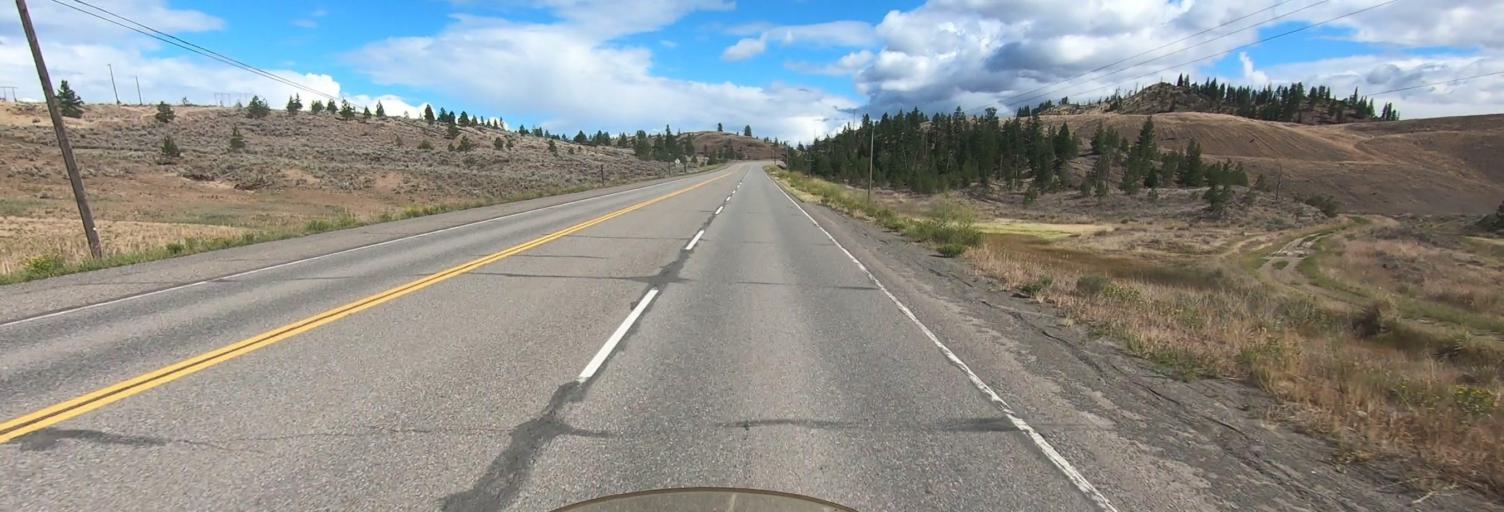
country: CA
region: British Columbia
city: Kamloops
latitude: 50.6622
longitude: -120.5465
